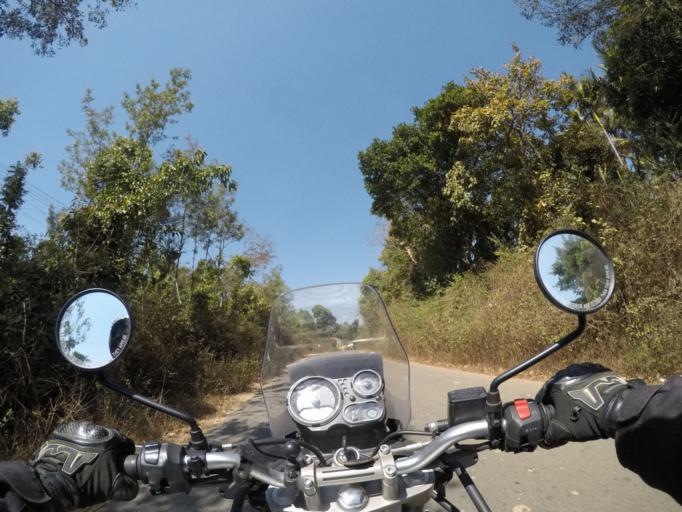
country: IN
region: Karnataka
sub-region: Chikmagalur
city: Mudigere
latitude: 13.0773
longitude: 75.6821
